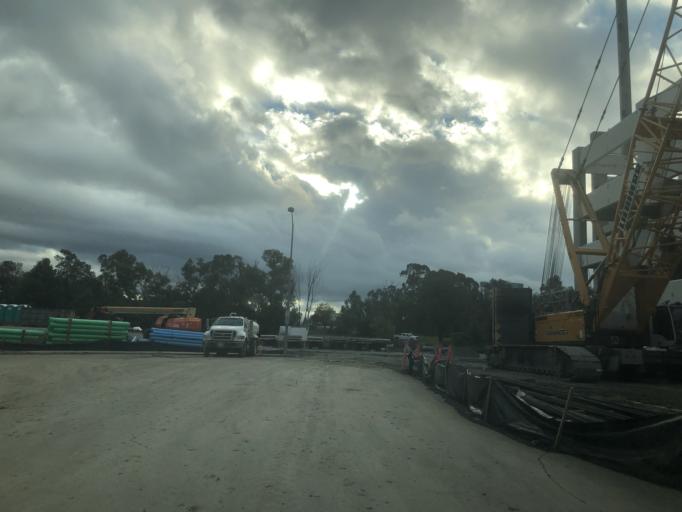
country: US
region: California
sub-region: Santa Clara County
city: San Jose
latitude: 37.3735
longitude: -121.9148
